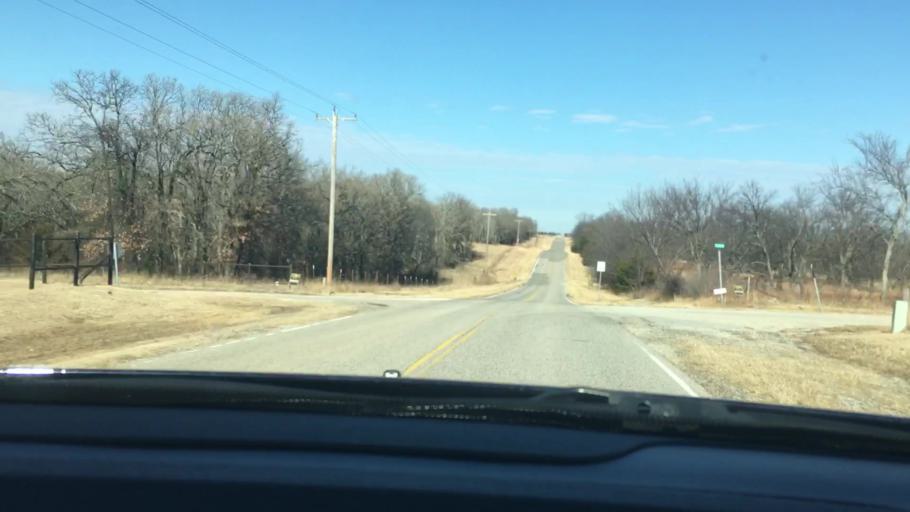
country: US
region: Oklahoma
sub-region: Garvin County
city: Wynnewood
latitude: 34.6657
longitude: -97.1254
